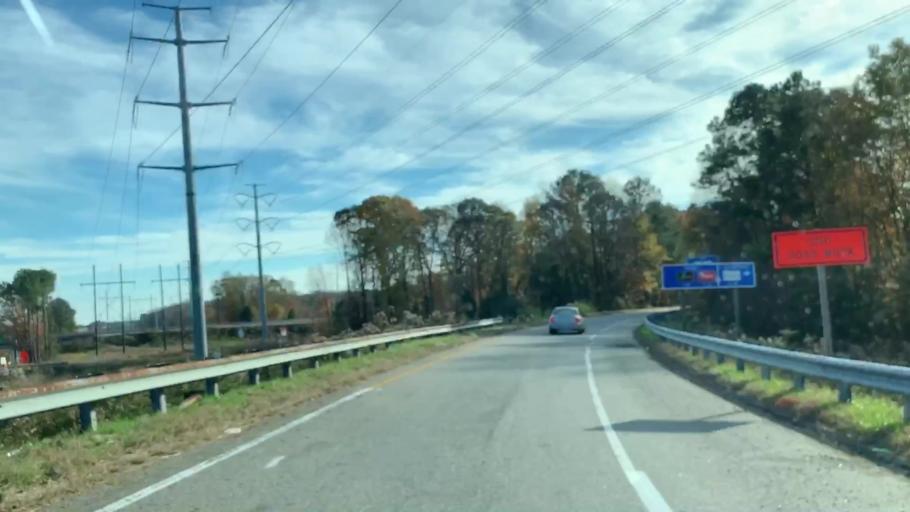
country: US
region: Virginia
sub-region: City of Williamsburg
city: Williamsburg
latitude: 37.2589
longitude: -76.6478
